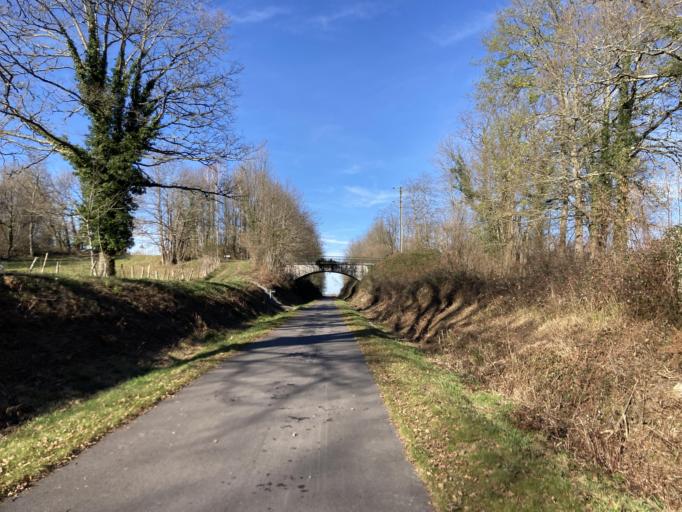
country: FR
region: Aquitaine
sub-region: Departement des Pyrenees-Atlantiques
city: Arudy
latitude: 43.1257
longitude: -0.4415
